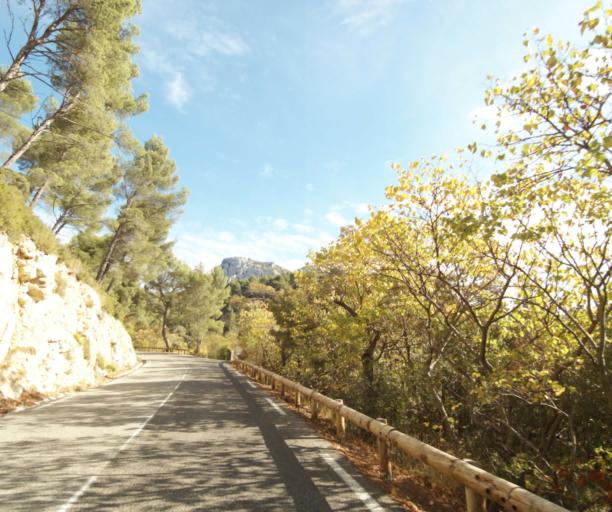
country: FR
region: Provence-Alpes-Cote d'Azur
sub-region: Departement des Bouches-du-Rhone
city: Gemenos
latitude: 43.2924
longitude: 5.6537
